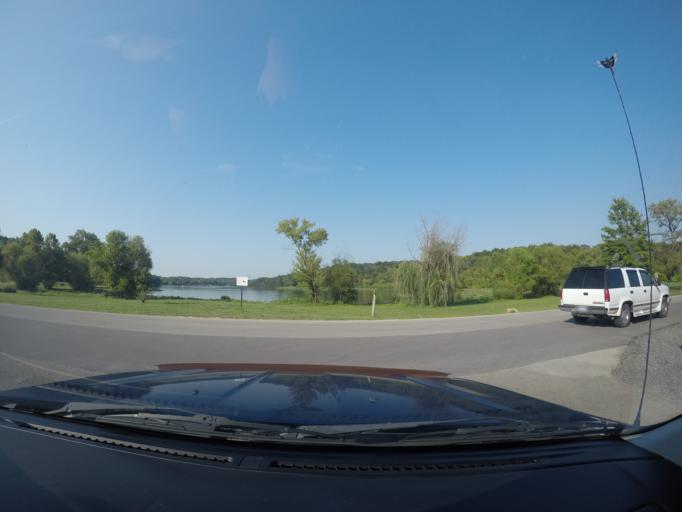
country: US
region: Kansas
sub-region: Wyandotte County
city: Edwardsville
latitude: 39.1504
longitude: -94.7890
